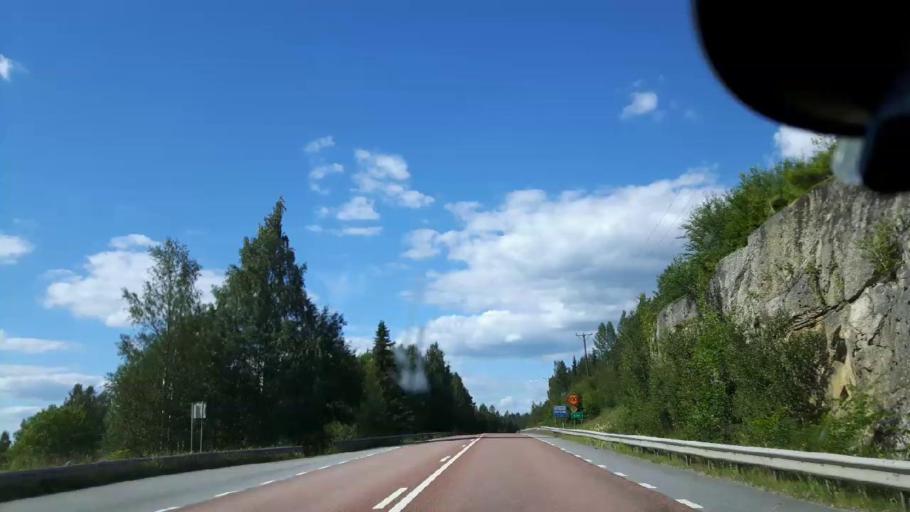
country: SE
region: Jaemtland
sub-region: Braecke Kommun
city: Braecke
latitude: 62.7919
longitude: 15.3769
